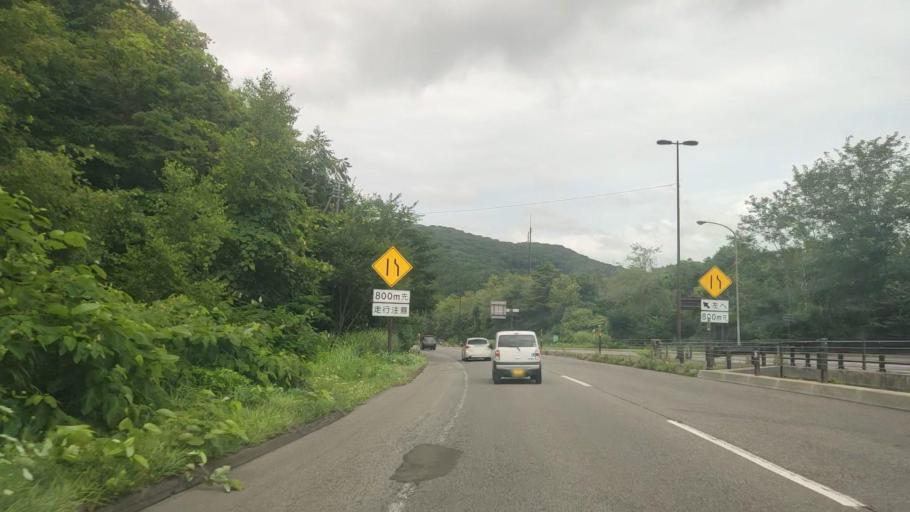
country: JP
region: Hokkaido
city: Nanae
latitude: 41.9577
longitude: 140.6498
